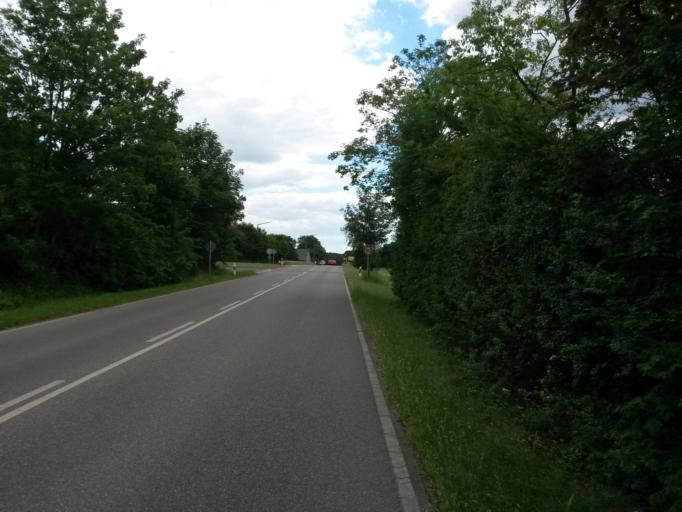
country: DE
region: Bavaria
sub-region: Regierungsbezirk Mittelfranken
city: Seukendorf
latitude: 49.4848
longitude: 10.8871
